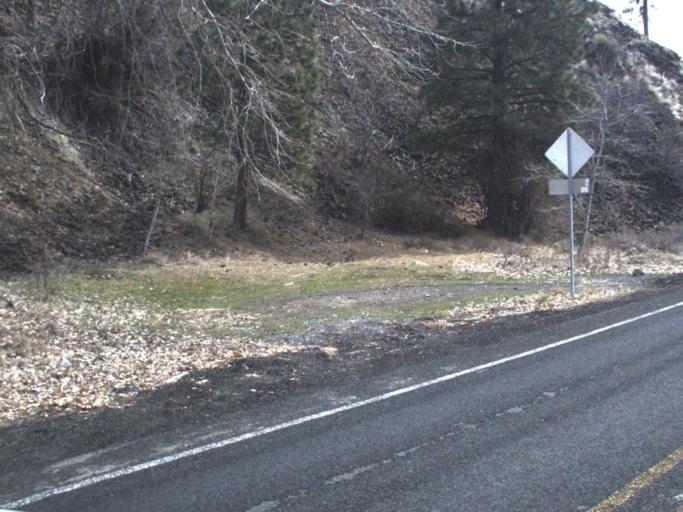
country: US
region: Washington
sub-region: Yakima County
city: Tieton
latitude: 46.8549
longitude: -120.9532
